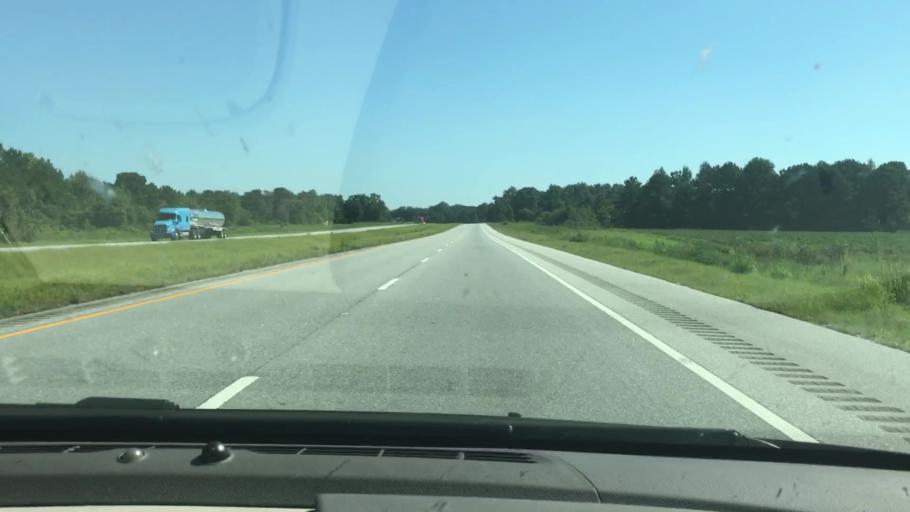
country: US
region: Alabama
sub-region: Russell County
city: Ladonia
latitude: 32.3623
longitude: -85.1025
